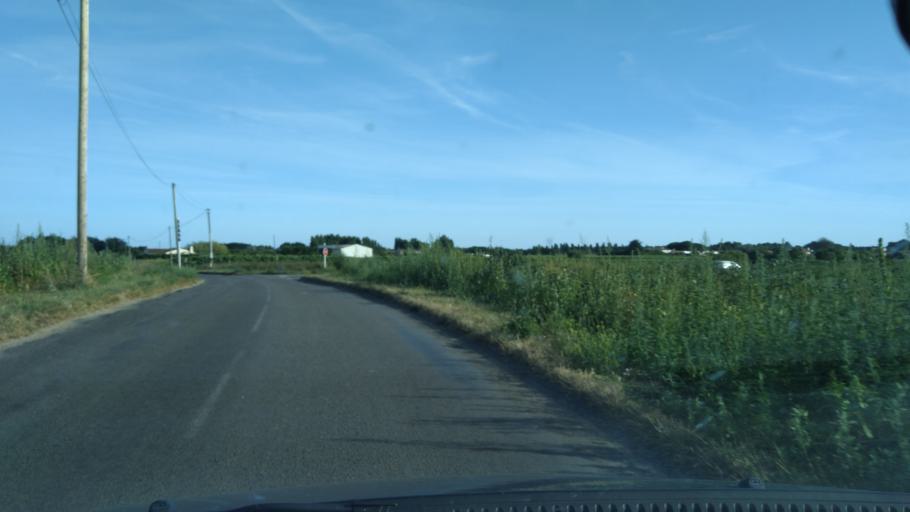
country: FR
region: Poitou-Charentes
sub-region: Departement de la Charente-Maritime
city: Dolus-d'Oleron
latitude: 45.9361
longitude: -1.3380
